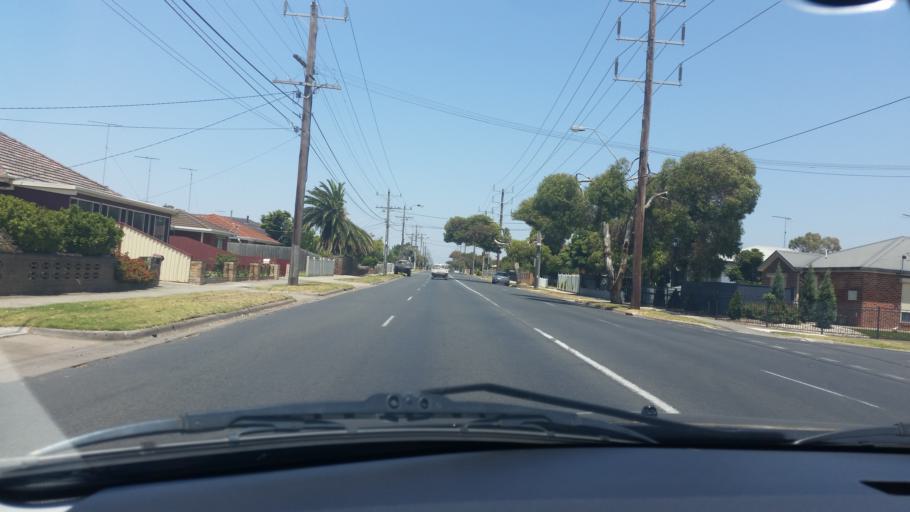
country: AU
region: Victoria
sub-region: Greater Geelong
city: Bell Park
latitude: -38.1125
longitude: 144.3431
